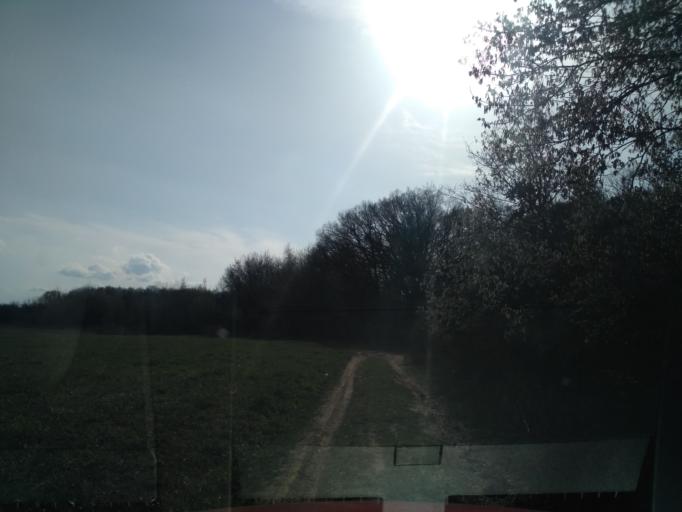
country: SK
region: Kosicky
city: Kosice
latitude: 48.6863
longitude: 21.1821
